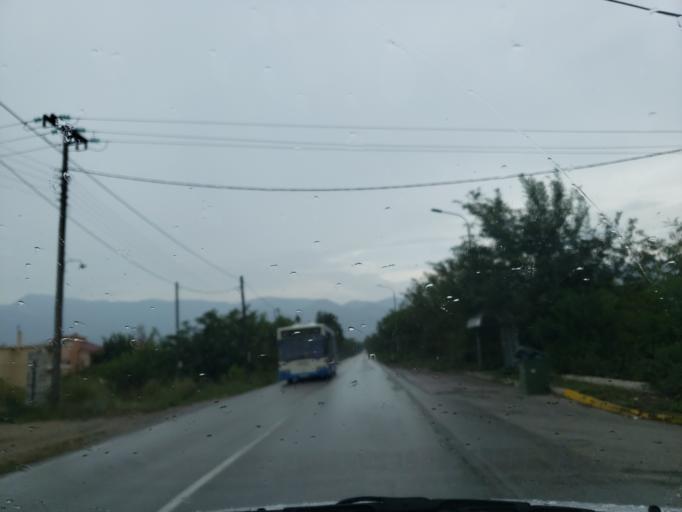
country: GR
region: Central Greece
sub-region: Nomos Fthiotidos
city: Anthili
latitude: 38.8340
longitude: 22.4413
